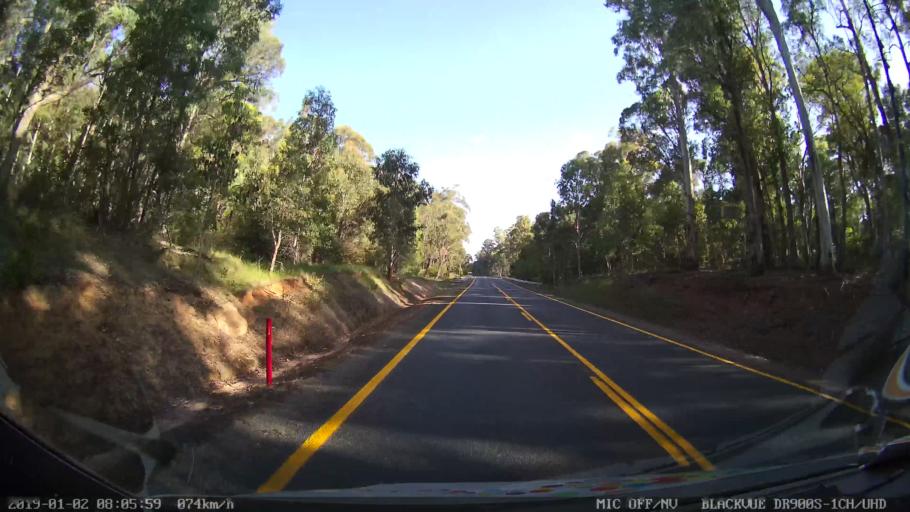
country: AU
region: New South Wales
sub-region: Tumut Shire
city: Tumut
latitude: -35.6452
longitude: 148.3872
